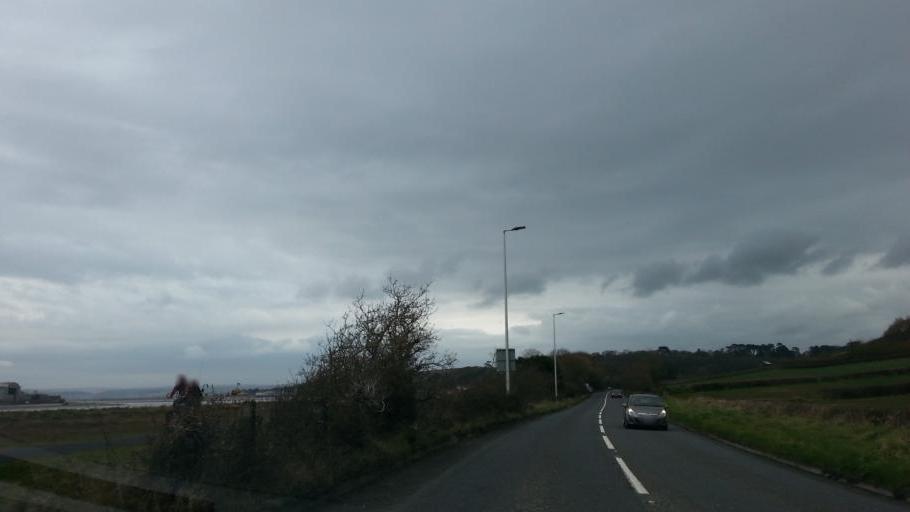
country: GB
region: England
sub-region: Devon
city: Appledore
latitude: 51.0343
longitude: -4.1948
